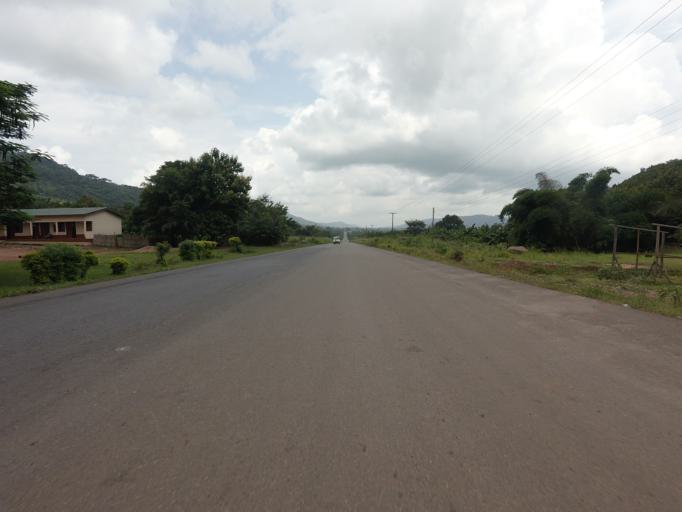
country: GH
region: Volta
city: Ho
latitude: 6.6213
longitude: 0.3075
